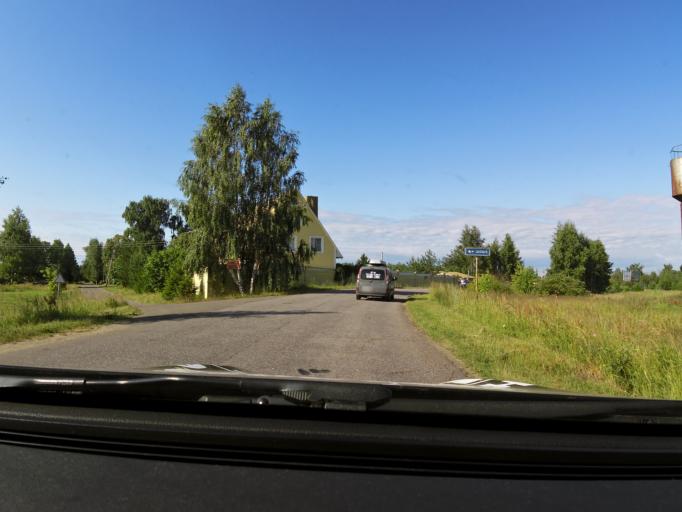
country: RU
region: Tverskaya
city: Zavidovo
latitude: 56.6083
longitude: 36.5457
